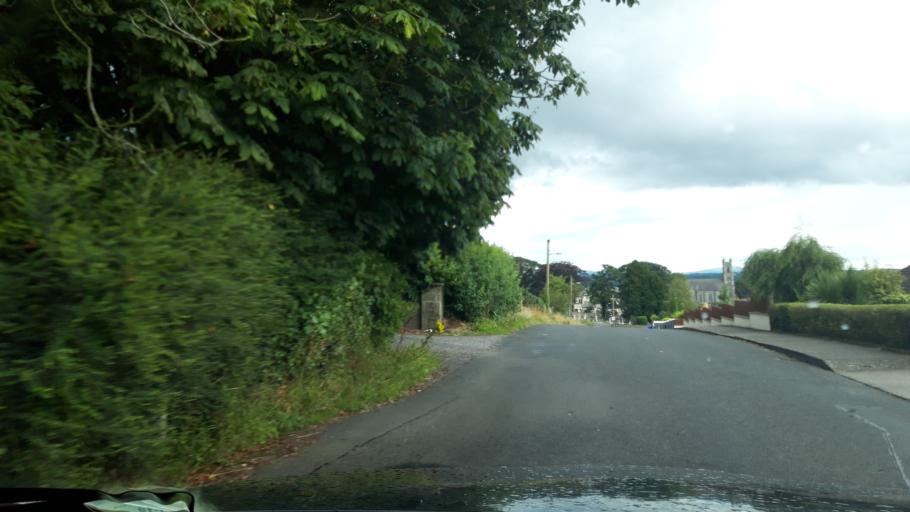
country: IE
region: Leinster
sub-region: Wicklow
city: Baltinglass
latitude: 52.9439
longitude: -6.7061
